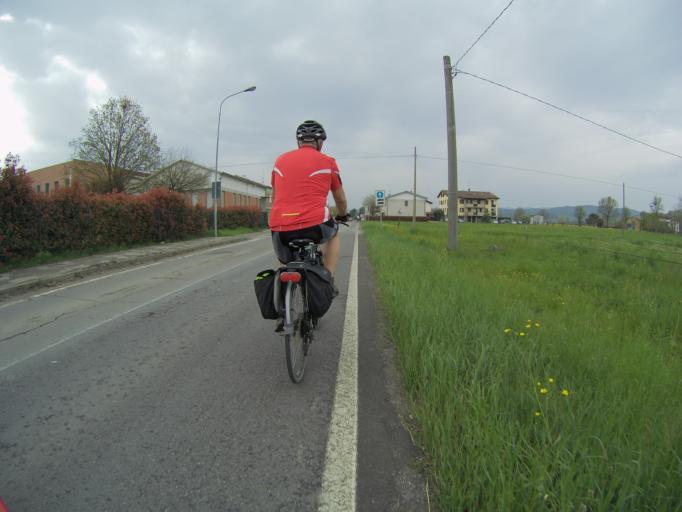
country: IT
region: Emilia-Romagna
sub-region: Provincia di Reggio Emilia
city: San Bartolomeo
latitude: 44.6536
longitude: 10.5251
